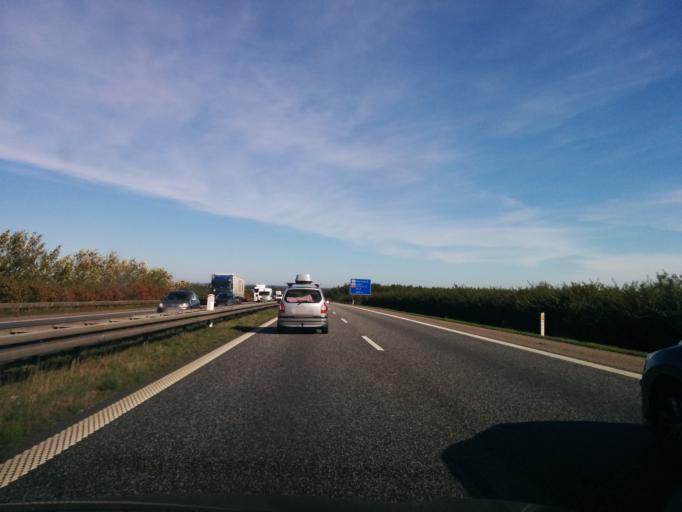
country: DK
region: Central Jutland
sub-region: Hedensted Kommune
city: Hedensted
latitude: 55.8365
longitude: 9.7240
